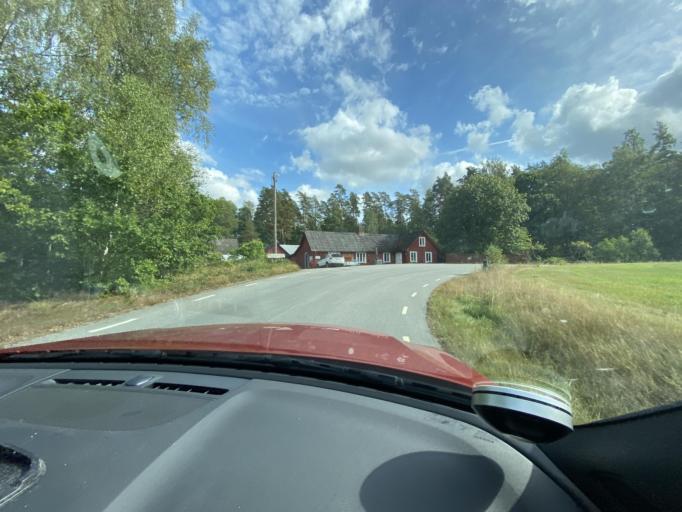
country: SE
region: Skane
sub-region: Hassleholms Kommun
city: Bjarnum
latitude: 56.3607
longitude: 13.8006
